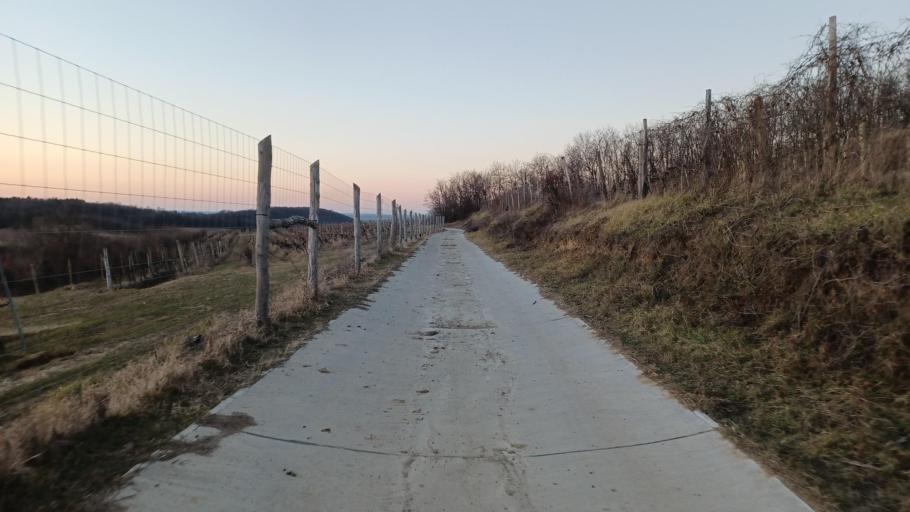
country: HU
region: Tolna
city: Szentgalpuszta
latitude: 46.3434
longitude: 18.6409
